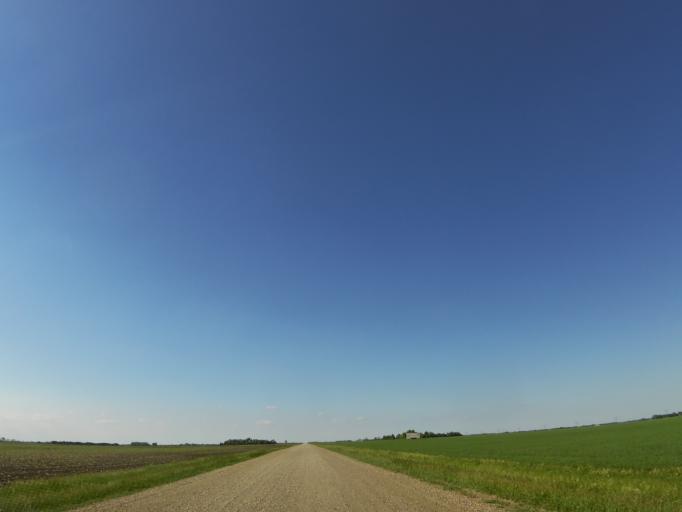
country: US
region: North Dakota
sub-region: Walsh County
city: Grafton
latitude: 48.3699
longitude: -97.2779
